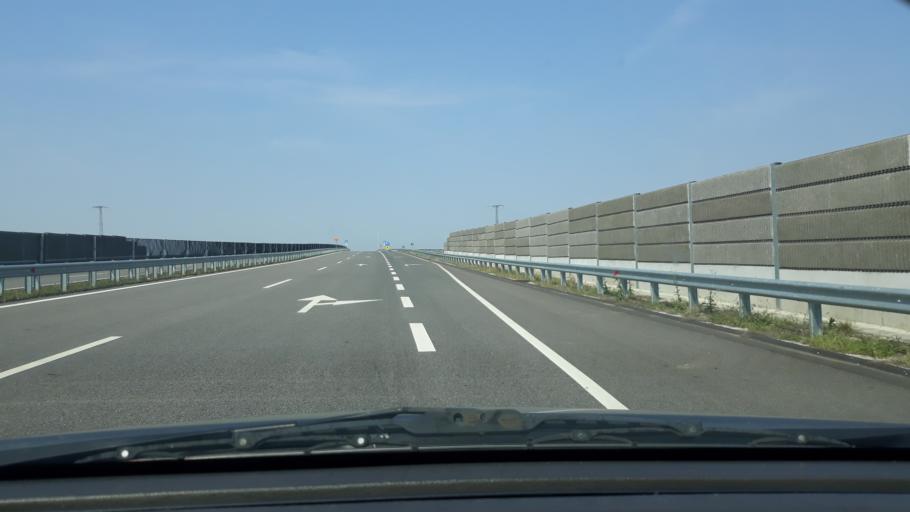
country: HU
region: Hajdu-Bihar
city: Berettyoujfalu
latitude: 47.2721
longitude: 21.5533
